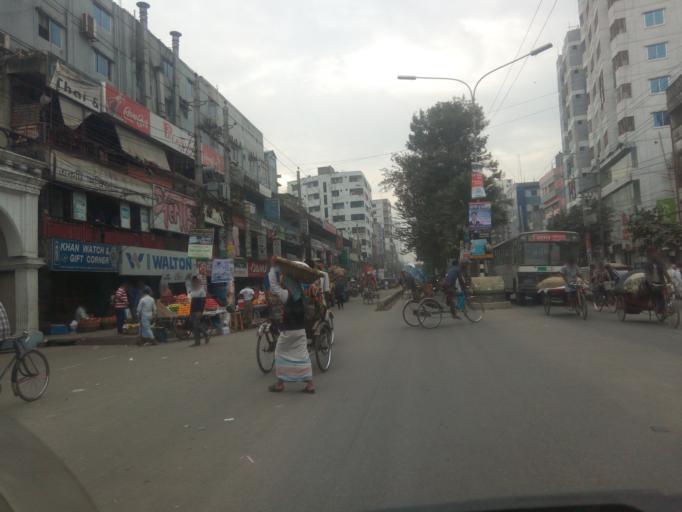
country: BD
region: Dhaka
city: Narayanganj
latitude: 23.6186
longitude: 90.5013
